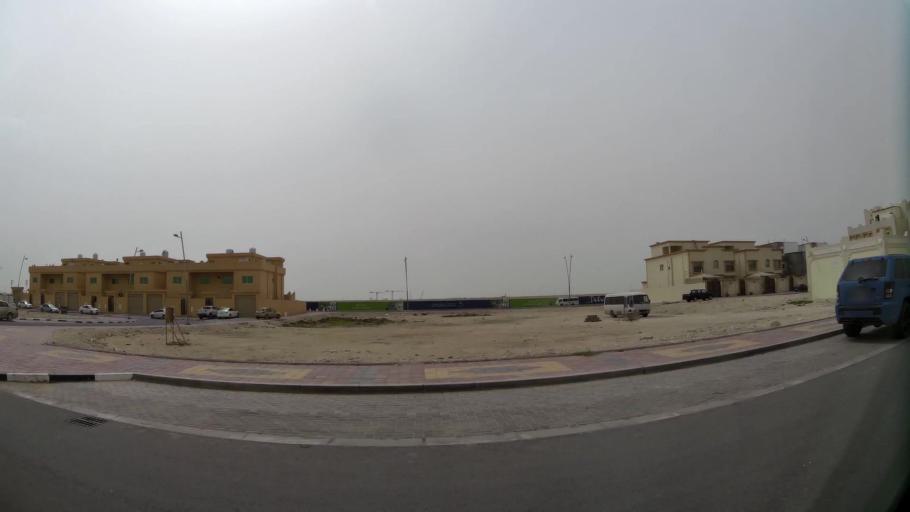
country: QA
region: Baladiyat ad Dawhah
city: Doha
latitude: 25.2356
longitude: 51.5354
